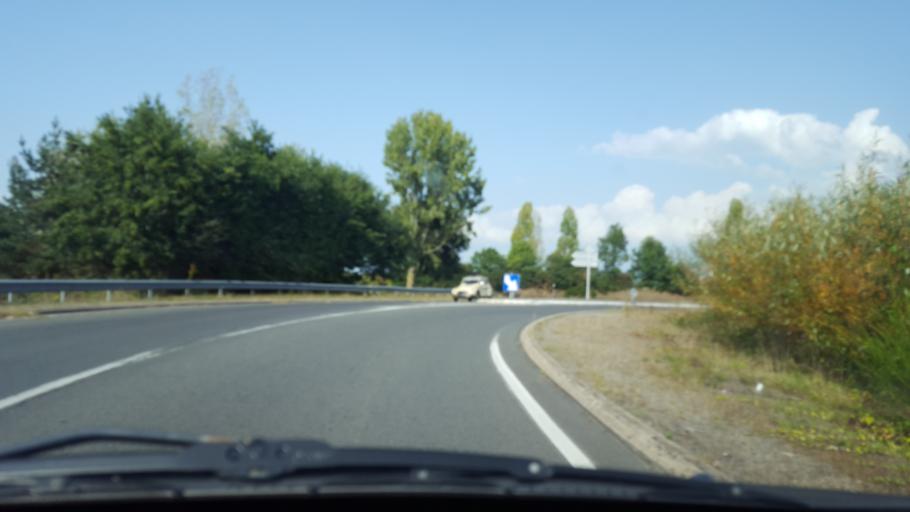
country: FR
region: Pays de la Loire
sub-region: Departement de la Loire-Atlantique
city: Saint-Philbert-de-Grand-Lieu
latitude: 47.0493
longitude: -1.6384
